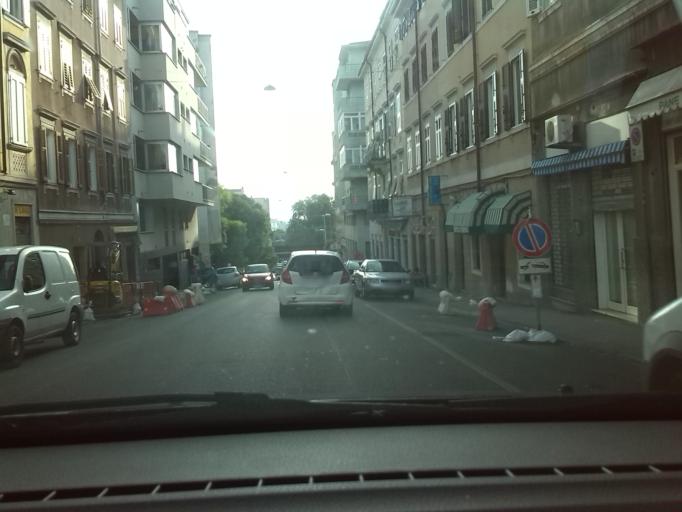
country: IT
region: Friuli Venezia Giulia
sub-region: Provincia di Trieste
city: Trieste
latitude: 45.6418
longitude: 13.7764
